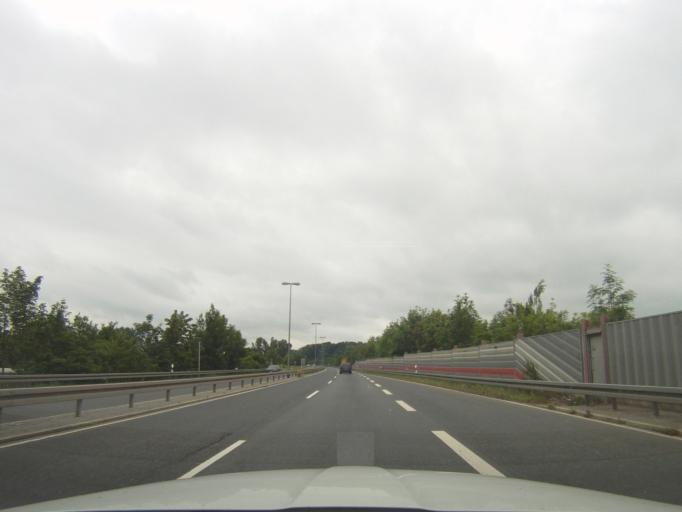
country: DE
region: Bavaria
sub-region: Upper Franconia
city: Coburg
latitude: 50.2741
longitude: 10.9556
